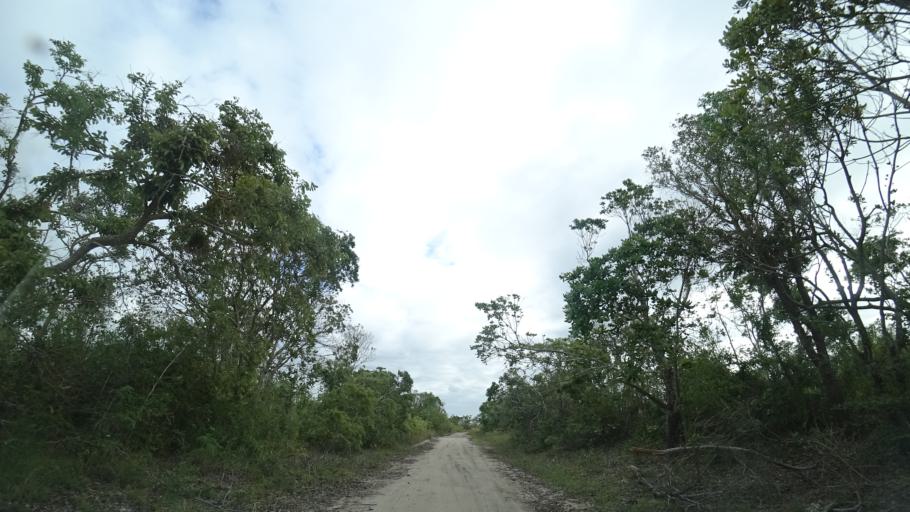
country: MZ
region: Sofala
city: Beira
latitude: -19.6124
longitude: 35.0761
